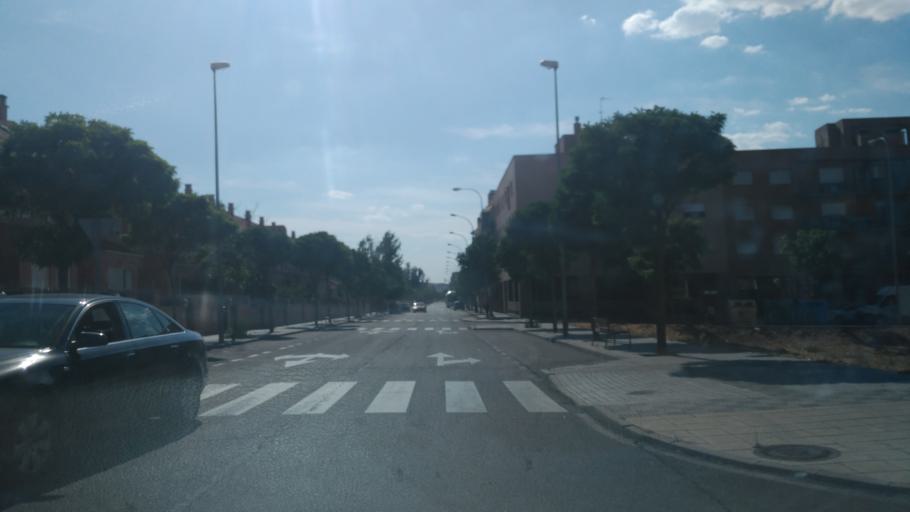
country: ES
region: Castille and Leon
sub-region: Provincia de Salamanca
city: Salamanca
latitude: 40.9564
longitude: -5.6798
